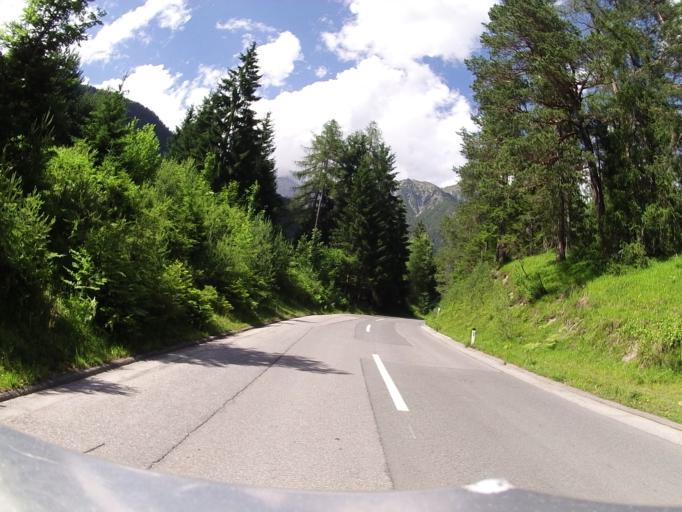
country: AT
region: Tyrol
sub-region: Politischer Bezirk Imst
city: Imst
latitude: 47.2666
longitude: 10.7418
